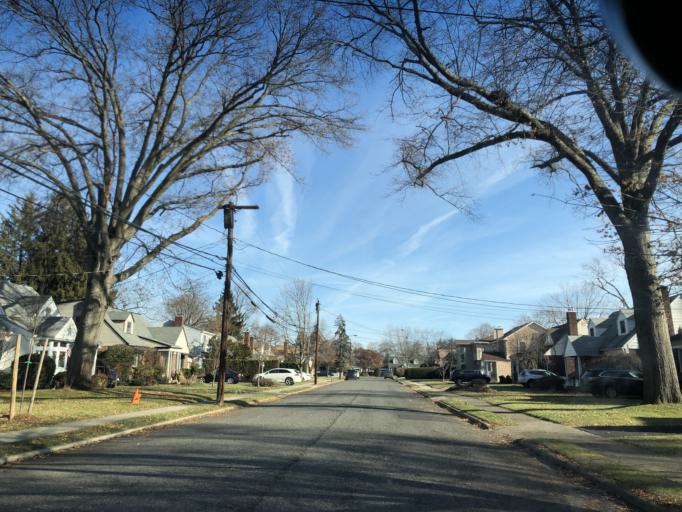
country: US
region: New Jersey
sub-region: Bergen County
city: Fair Lawn
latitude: 40.9261
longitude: -74.1239
